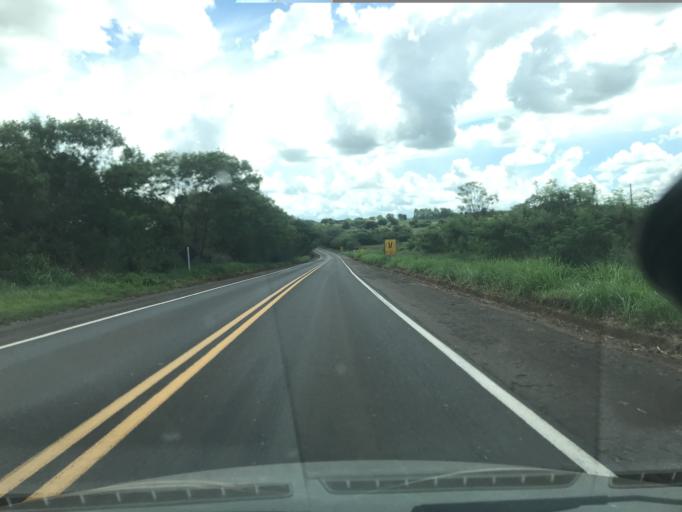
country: BR
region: Parana
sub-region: Cruzeiro Do Oeste
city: Cruzeiro do Oeste
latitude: -23.7890
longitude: -53.0301
